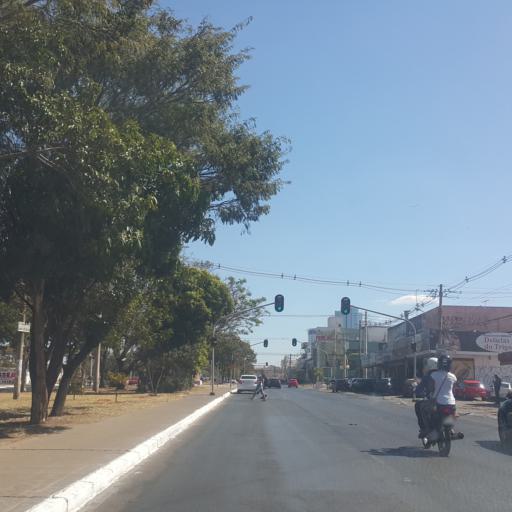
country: BR
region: Federal District
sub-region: Brasilia
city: Brasilia
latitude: -15.8076
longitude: -48.0823
